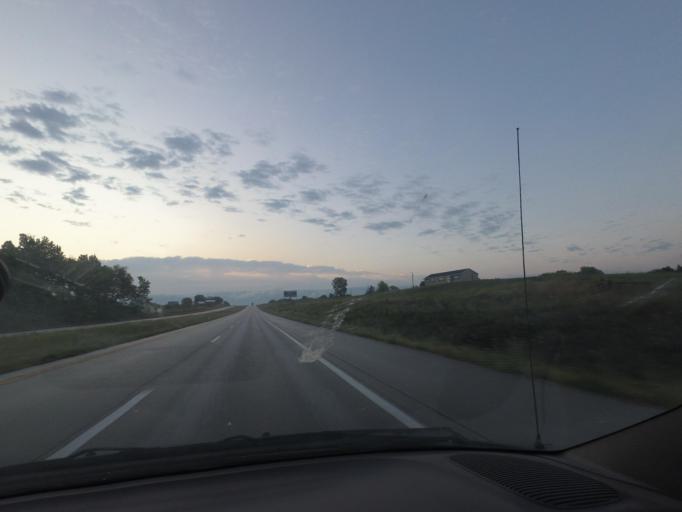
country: US
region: Missouri
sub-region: Macon County
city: Macon
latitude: 39.7556
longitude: -92.5408
